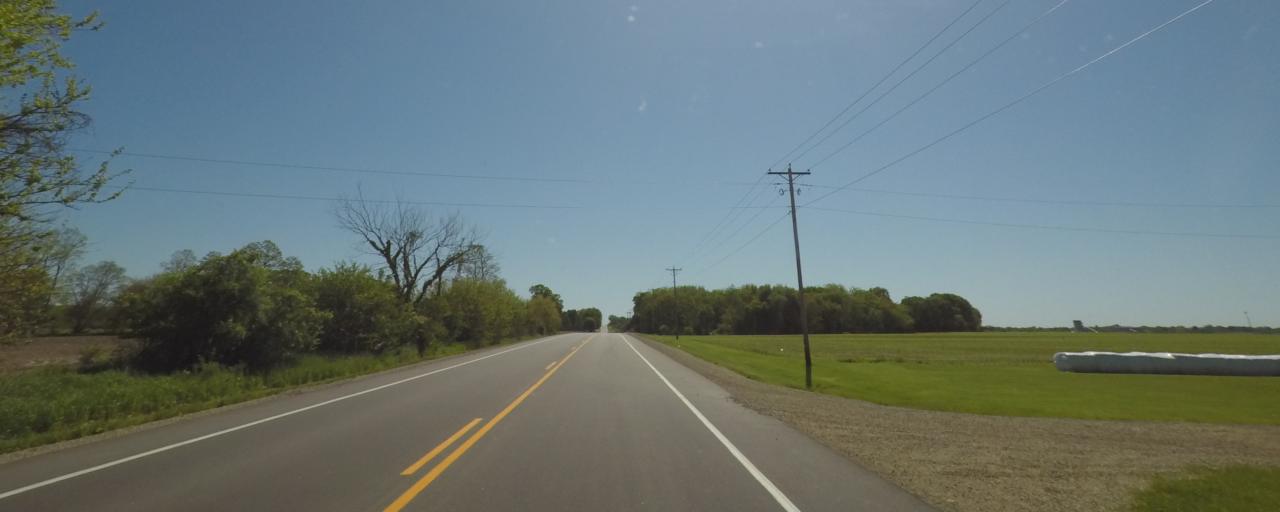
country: US
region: Wisconsin
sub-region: Dane County
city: Oregon
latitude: 42.9504
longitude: -89.4051
